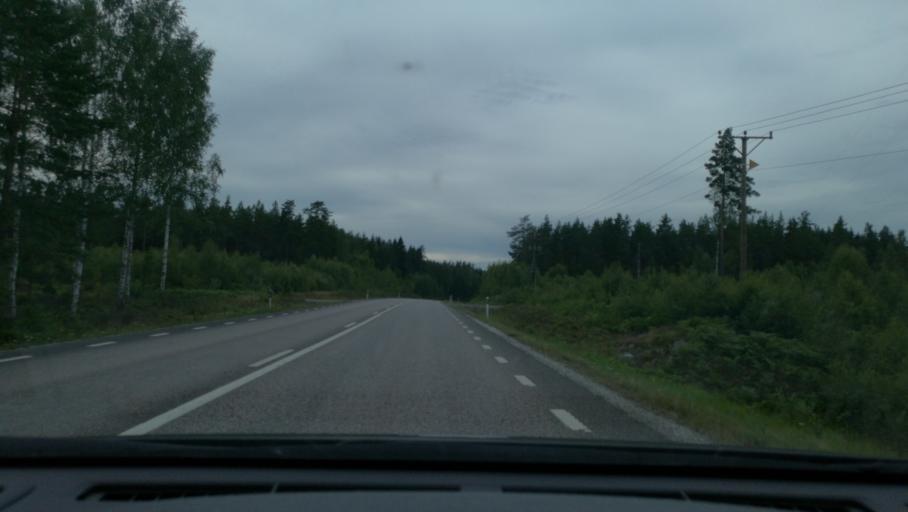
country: SE
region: Soedermanland
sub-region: Katrineholms Kommun
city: Katrineholm
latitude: 59.0834
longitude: 16.2022
